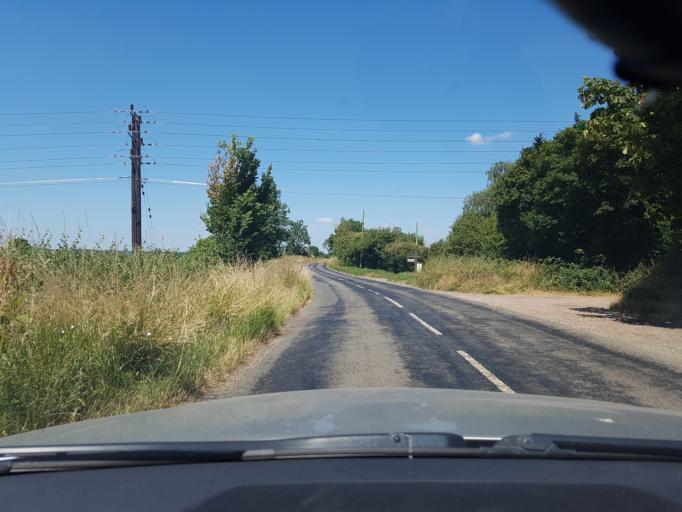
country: GB
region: England
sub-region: Milton Keynes
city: Calverton
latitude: 52.0362
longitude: -0.8406
